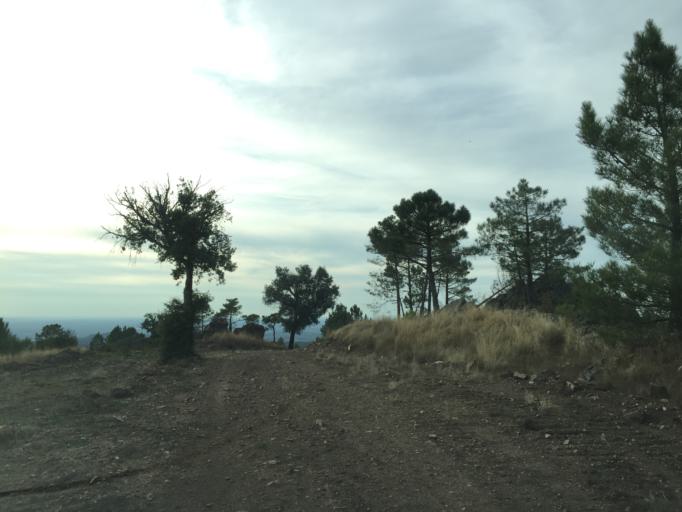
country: PT
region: Portalegre
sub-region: Portalegre
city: Reguengo
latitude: 39.3148
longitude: -7.3635
